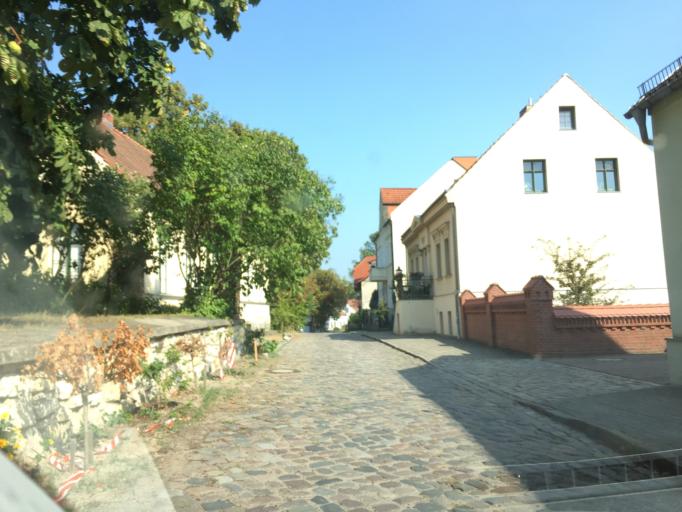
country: DE
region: Berlin
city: Rahnsdorf
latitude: 52.4306
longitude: 13.6889
